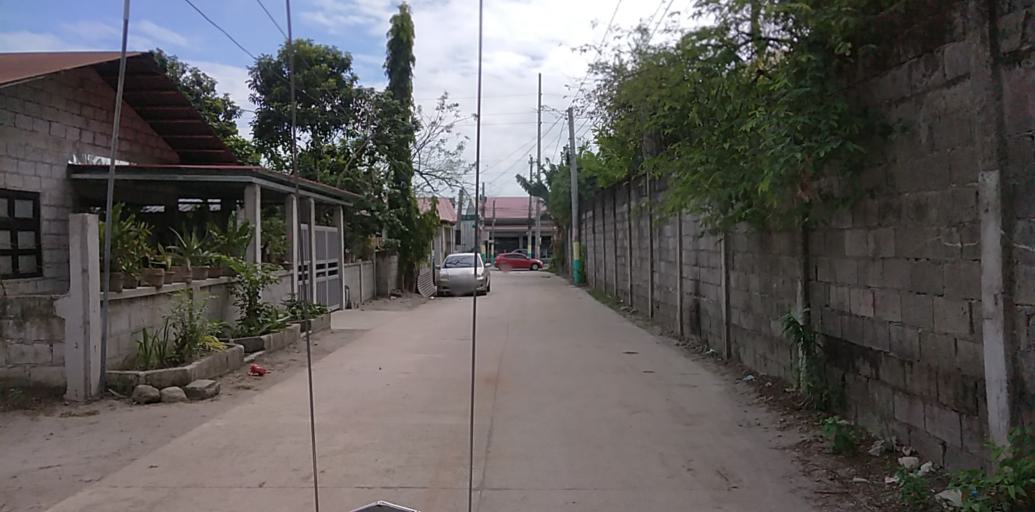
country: PH
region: Central Luzon
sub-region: Province of Pampanga
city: Porac
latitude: 15.0630
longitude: 120.5413
